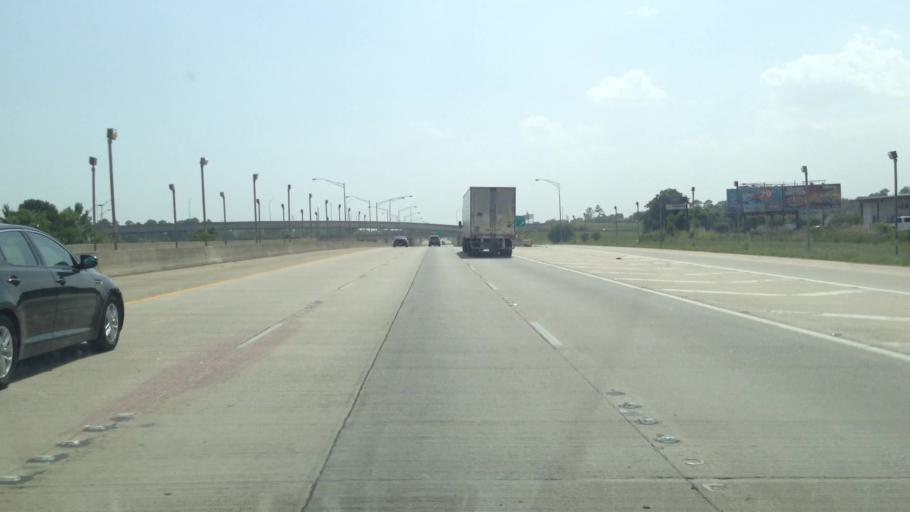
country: US
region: Louisiana
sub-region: Caddo Parish
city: Shreveport
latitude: 32.4578
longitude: -93.8397
